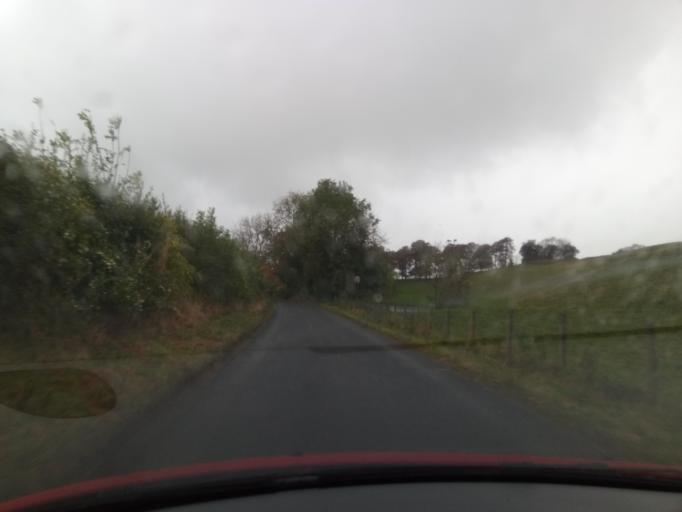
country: GB
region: Scotland
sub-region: The Scottish Borders
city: Selkirk
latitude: 55.5119
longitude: -2.7885
